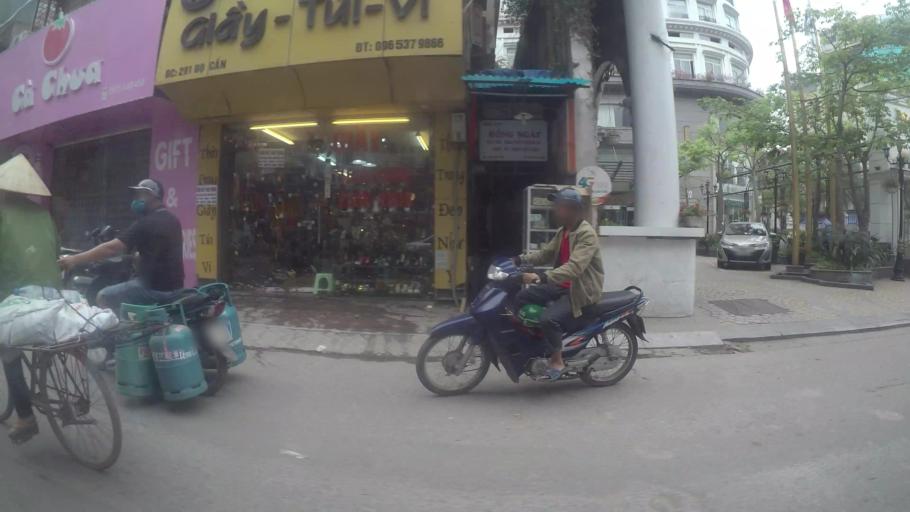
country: VN
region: Ha Noi
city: Cau Giay
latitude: 21.0355
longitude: 105.8185
